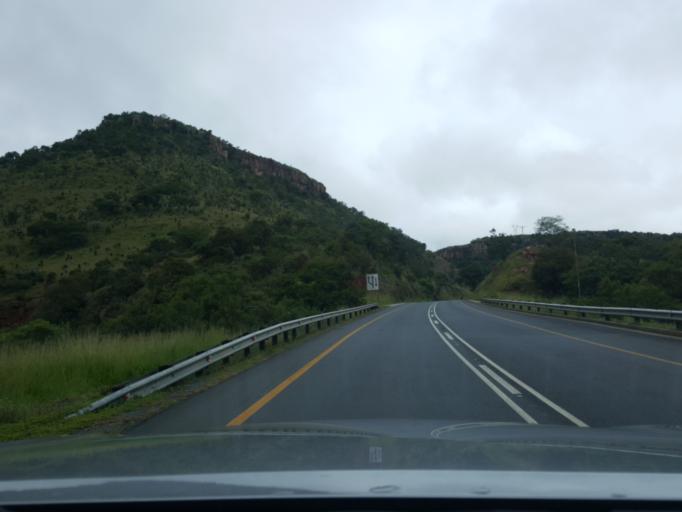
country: ZA
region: Mpumalanga
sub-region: Nkangala District Municipality
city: Belfast
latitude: -25.6449
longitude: 30.3546
